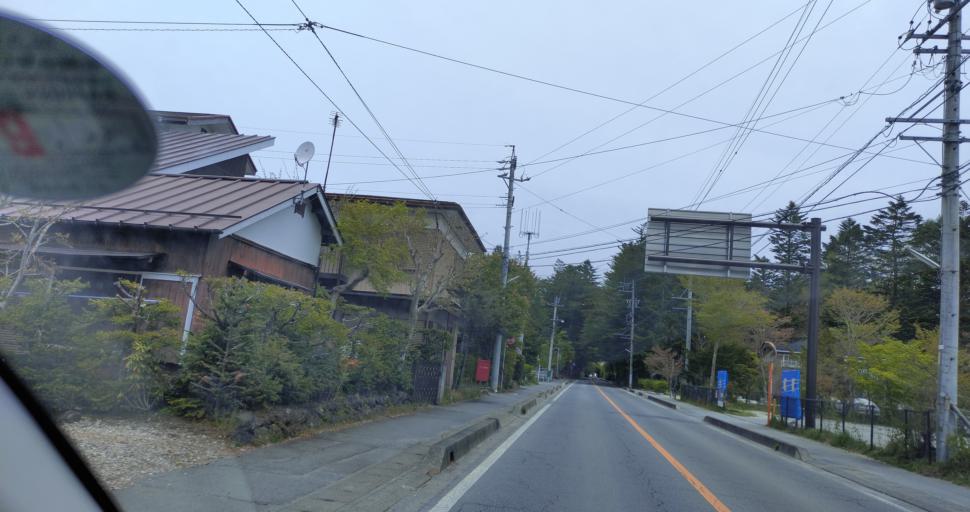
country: JP
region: Nagano
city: Saku
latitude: 36.3508
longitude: 138.6303
